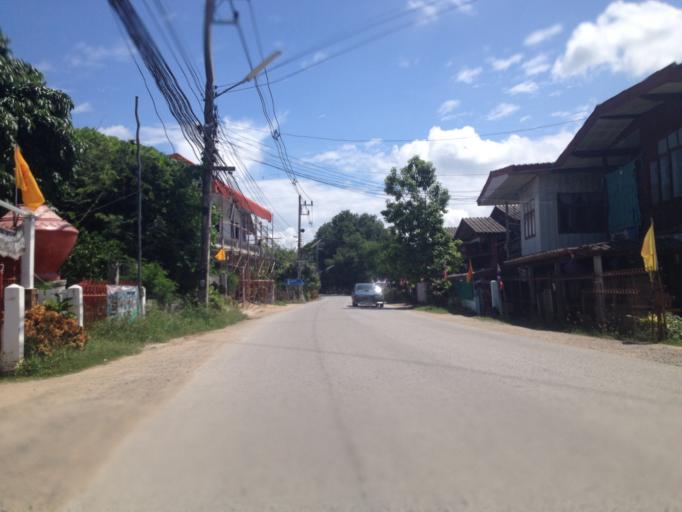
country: TH
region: Chiang Mai
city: San Pa Tong
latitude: 18.6418
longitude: 98.9286
